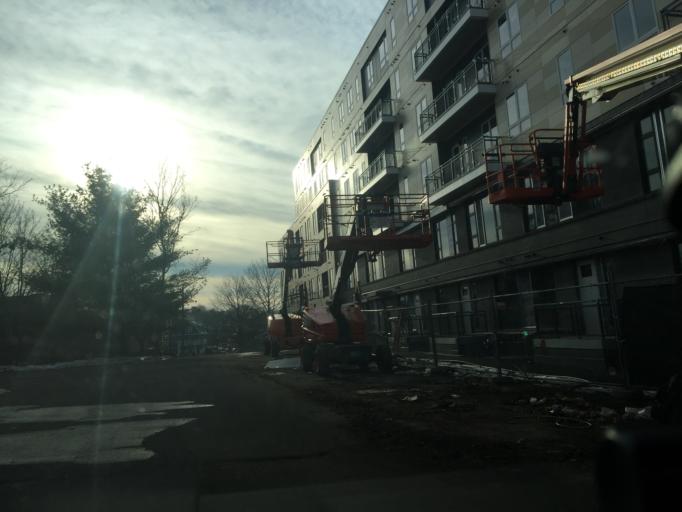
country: US
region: Massachusetts
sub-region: Norfolk County
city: Brookline
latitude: 42.3472
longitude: -71.1447
